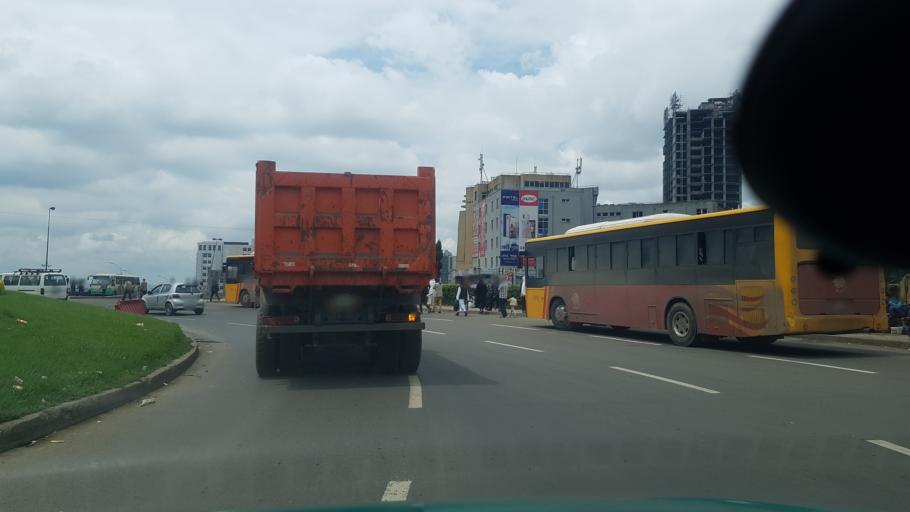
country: ET
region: Adis Abeba
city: Addis Ababa
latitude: 9.0216
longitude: 38.8010
